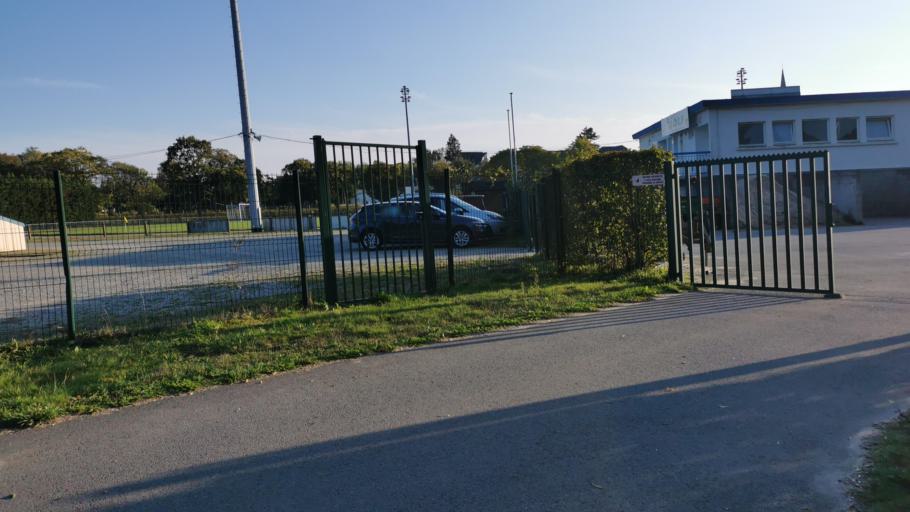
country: FR
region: Pays de la Loire
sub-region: Departement de la Loire-Atlantique
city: Saint-Sebastien-sur-Loire
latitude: 47.2120
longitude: -1.5007
